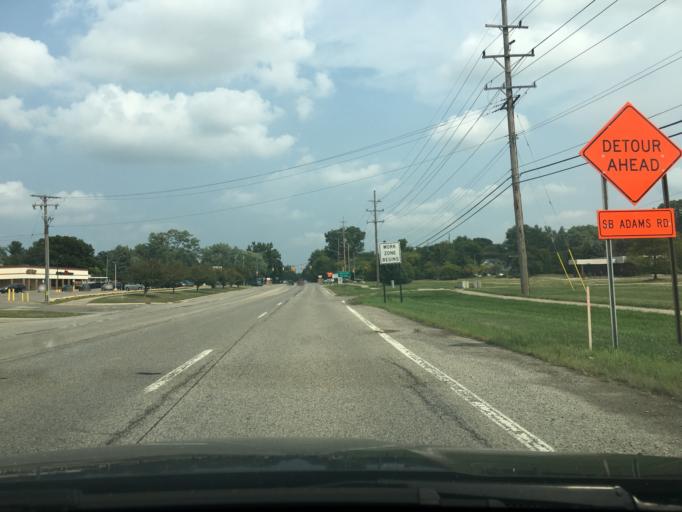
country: US
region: Michigan
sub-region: Oakland County
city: Bloomfield Hills
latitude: 42.6205
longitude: -83.2265
